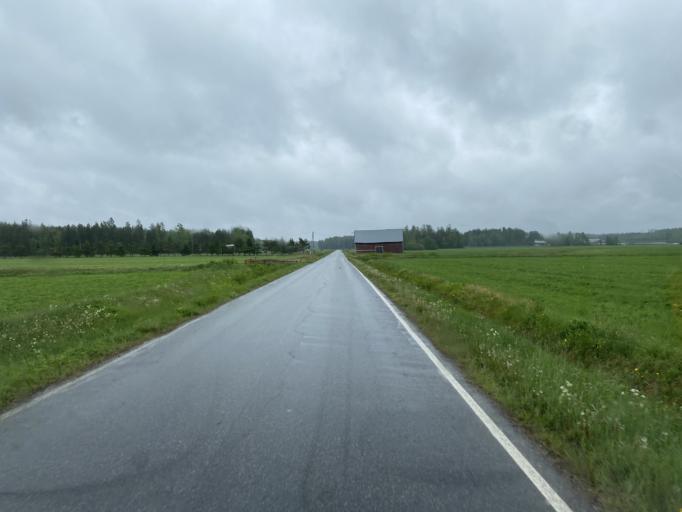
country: FI
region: Haeme
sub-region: Forssa
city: Humppila
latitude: 61.0534
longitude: 23.3361
